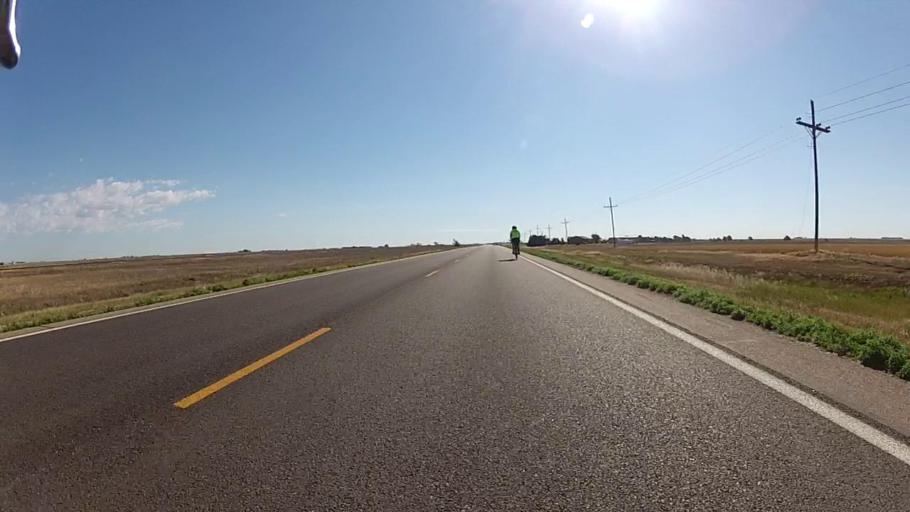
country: US
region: Kansas
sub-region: Gray County
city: Cimarron
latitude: 37.5760
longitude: -100.5241
